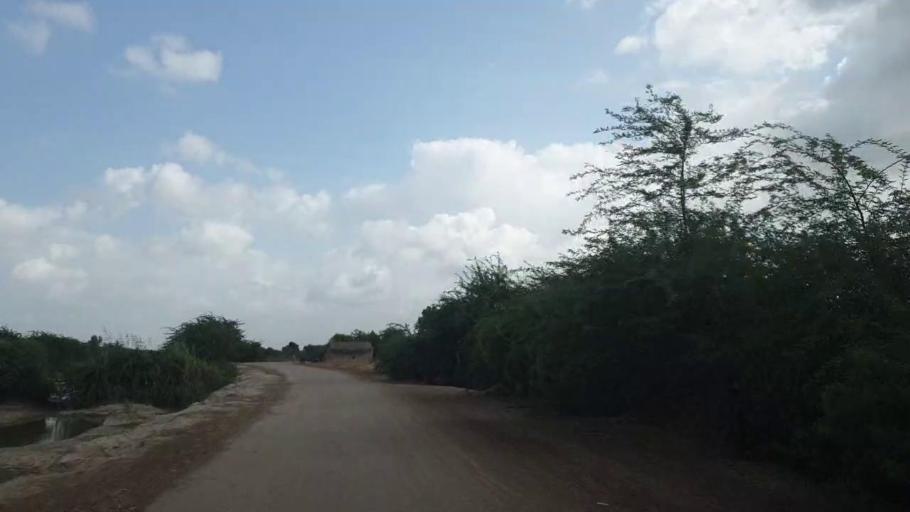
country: PK
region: Sindh
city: Kadhan
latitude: 24.5509
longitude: 69.0634
